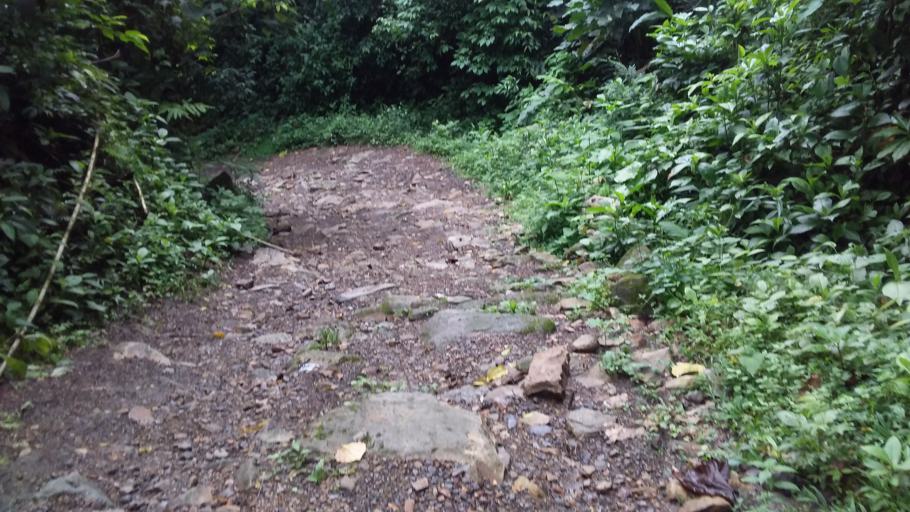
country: CO
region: Casanare
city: Nunchia
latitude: 5.6458
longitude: -72.2957
